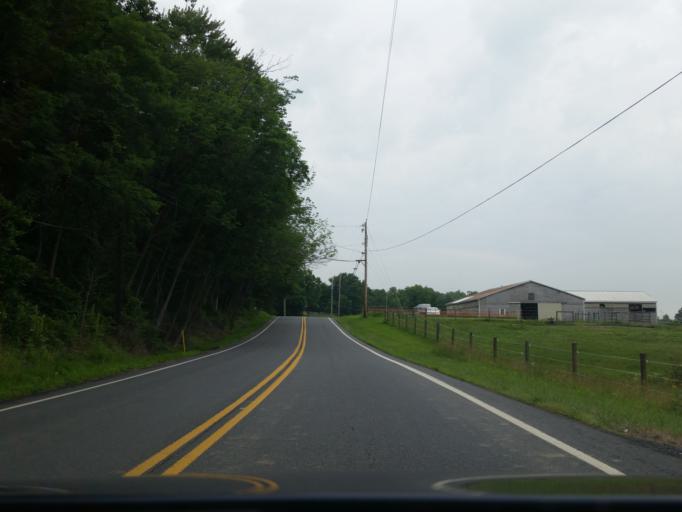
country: US
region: Pennsylvania
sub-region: Dauphin County
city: Skyline View
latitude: 40.3980
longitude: -76.6725
